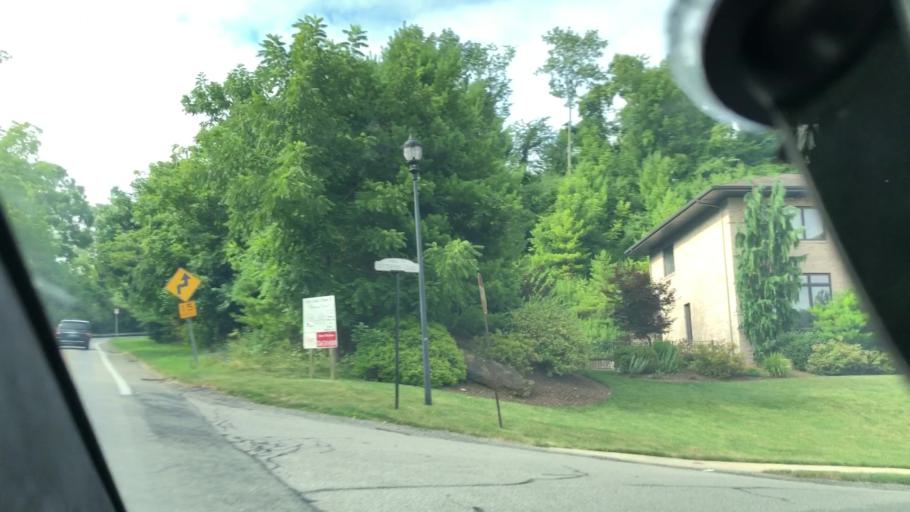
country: US
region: Pennsylvania
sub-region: Allegheny County
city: Mount Lebanon
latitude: 40.3576
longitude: -80.0717
